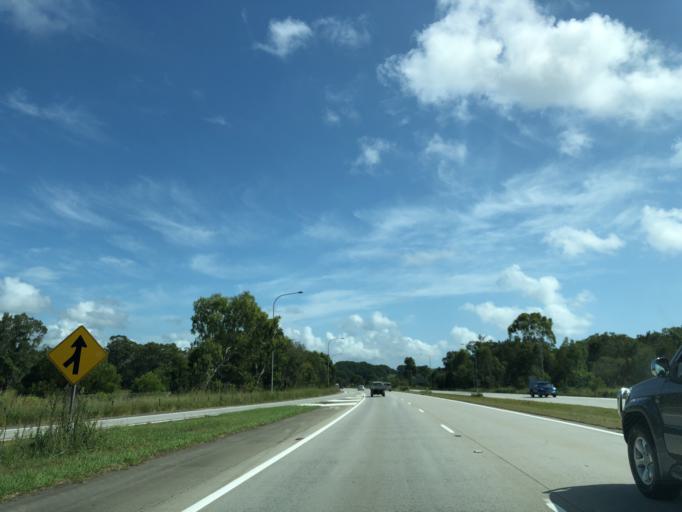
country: AU
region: New South Wales
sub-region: Byron Shire
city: Brunswick Heads
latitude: -28.5825
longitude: 153.5445
